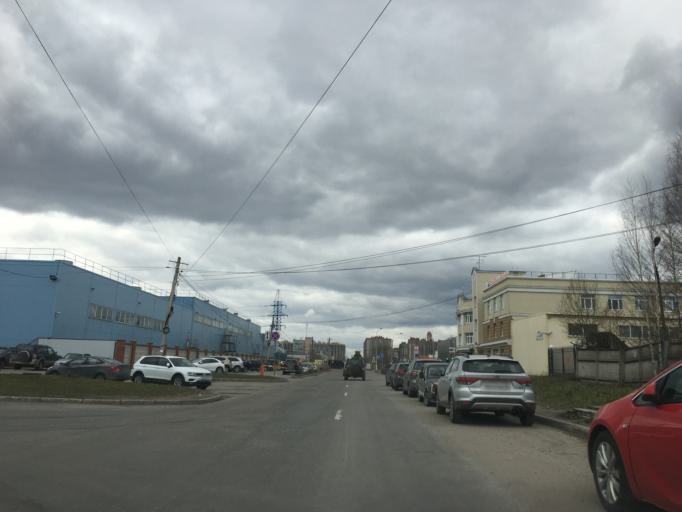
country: RU
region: Leningrad
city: Bugry
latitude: 60.0691
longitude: 30.3754
